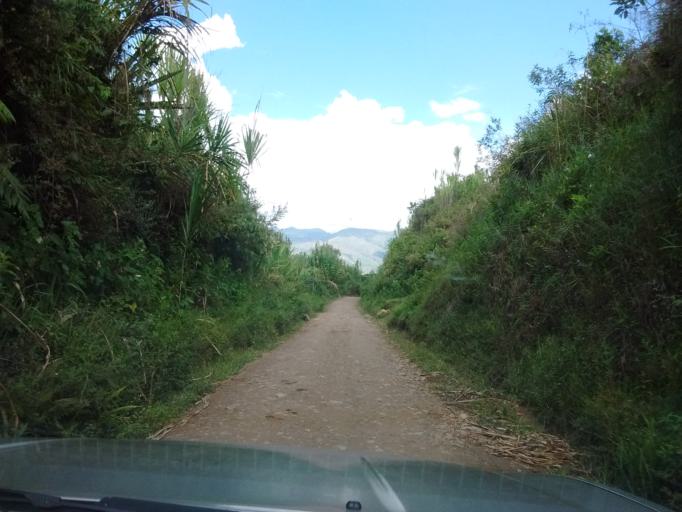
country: CO
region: Cauca
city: Morales
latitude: 2.6880
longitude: -76.7382
